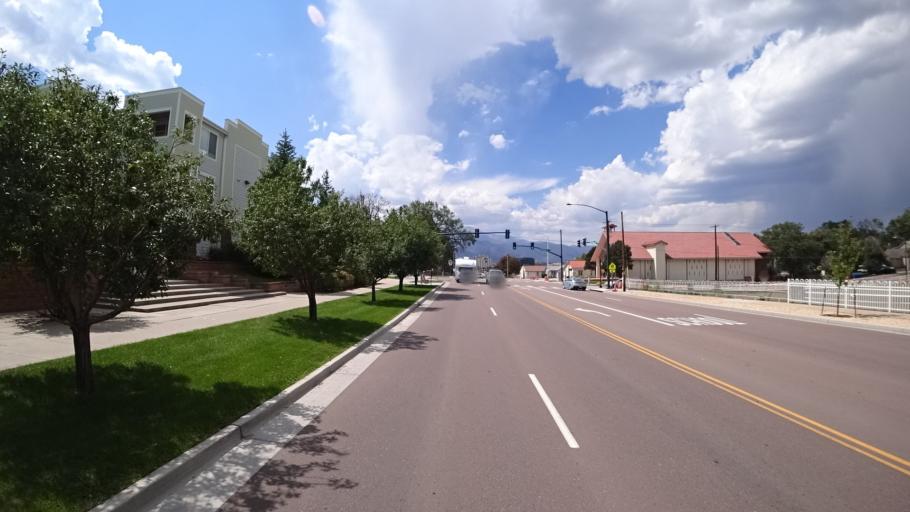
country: US
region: Colorado
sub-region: El Paso County
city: Colorado Springs
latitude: 38.8333
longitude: -104.8076
